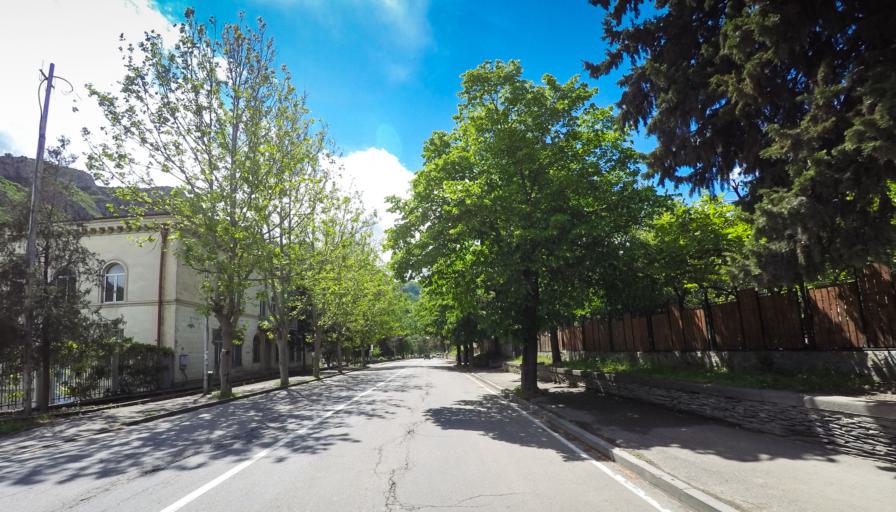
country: GE
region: Mtskheta-Mtianeti
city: Mtskheta
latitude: 41.8400
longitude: 44.7125
